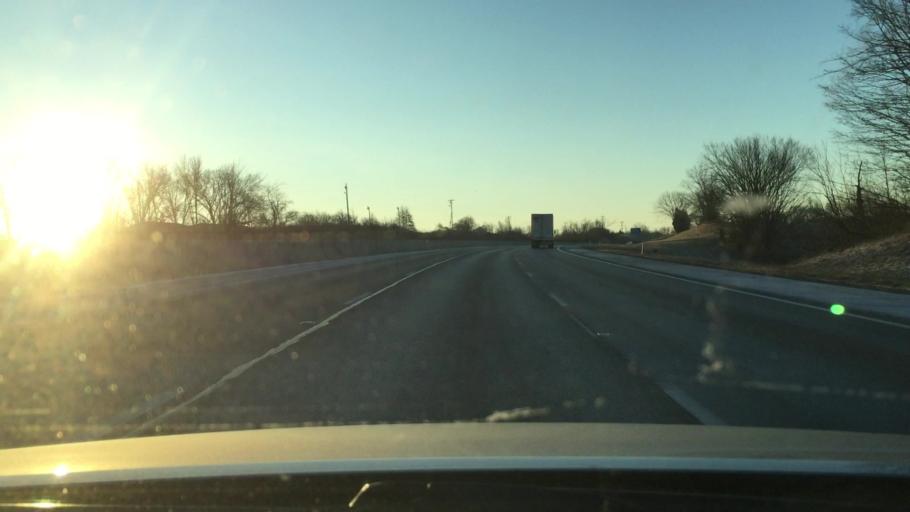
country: US
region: Kentucky
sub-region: Grant County
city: Dry Ridge
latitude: 38.6640
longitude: -84.5889
